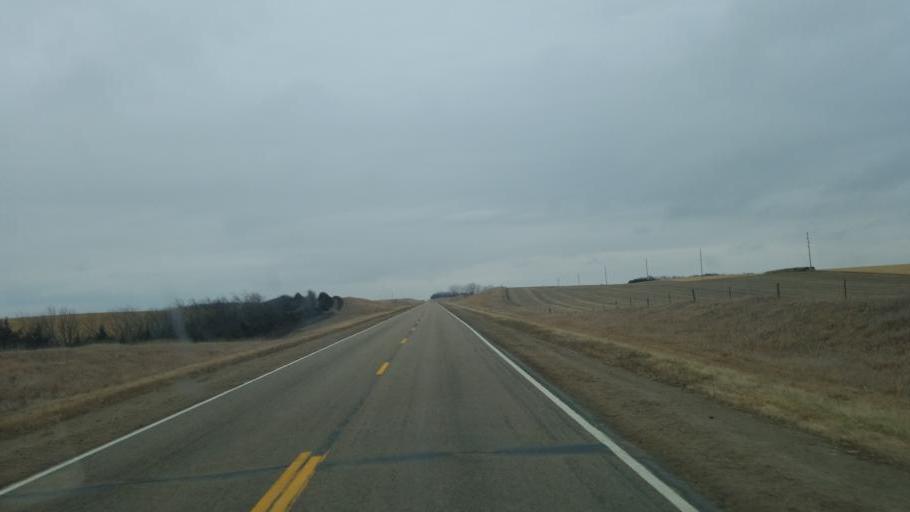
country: US
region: Nebraska
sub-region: Knox County
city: Bloomfield
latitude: 42.5978
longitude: -97.5905
